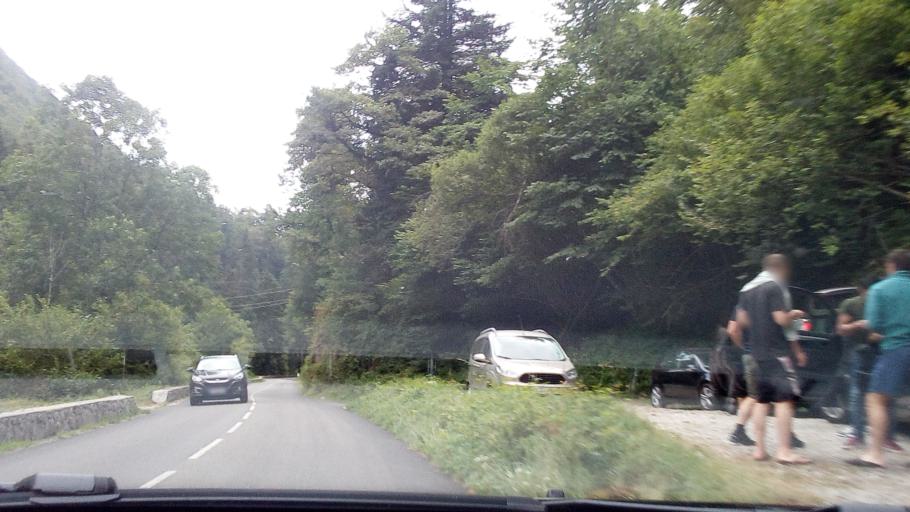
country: FR
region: Aquitaine
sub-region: Departement des Pyrenees-Atlantiques
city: Laruns
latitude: 42.9298
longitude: -0.4484
